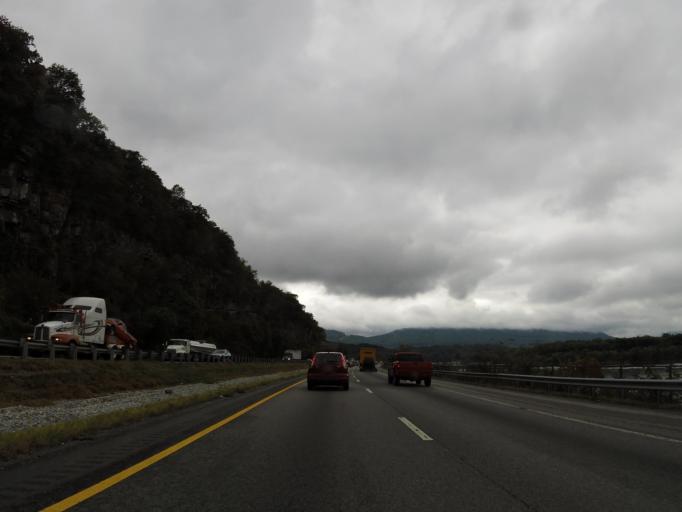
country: US
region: Tennessee
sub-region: Hamilton County
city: Lookout Mountain
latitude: 35.0213
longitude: -85.3381
